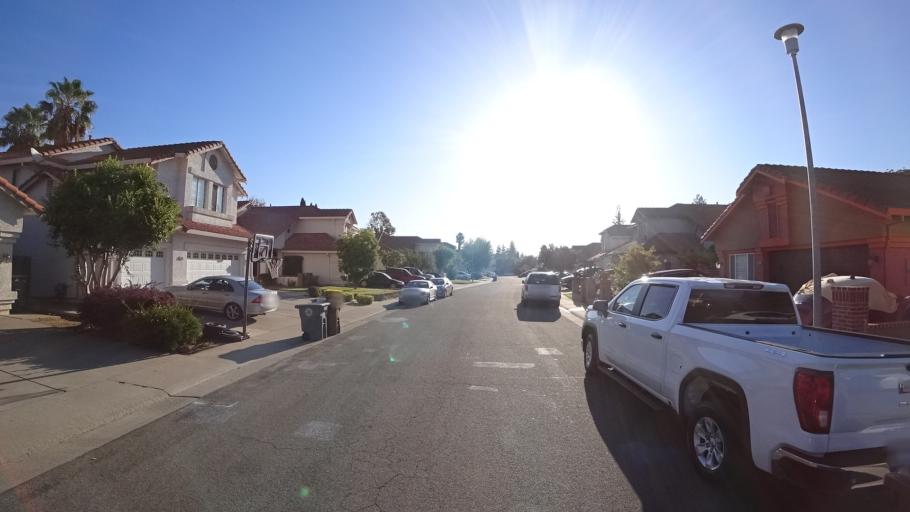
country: US
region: California
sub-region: Sacramento County
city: Laguna
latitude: 38.4323
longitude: -121.4527
